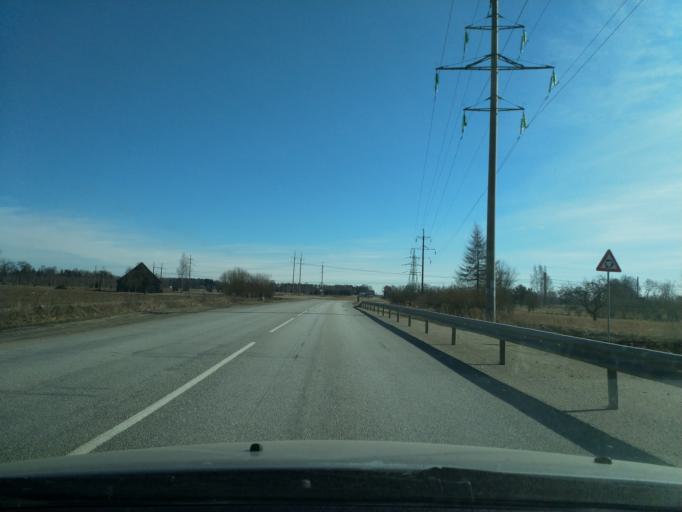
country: LV
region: Valmieras Rajons
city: Valmiera
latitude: 57.5100
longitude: 25.4457
